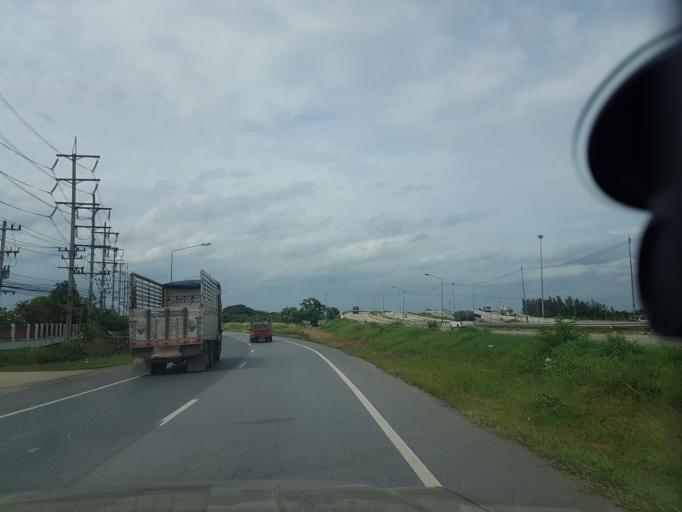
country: TH
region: Sara Buri
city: Saraburi
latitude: 14.5610
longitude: 100.9025
